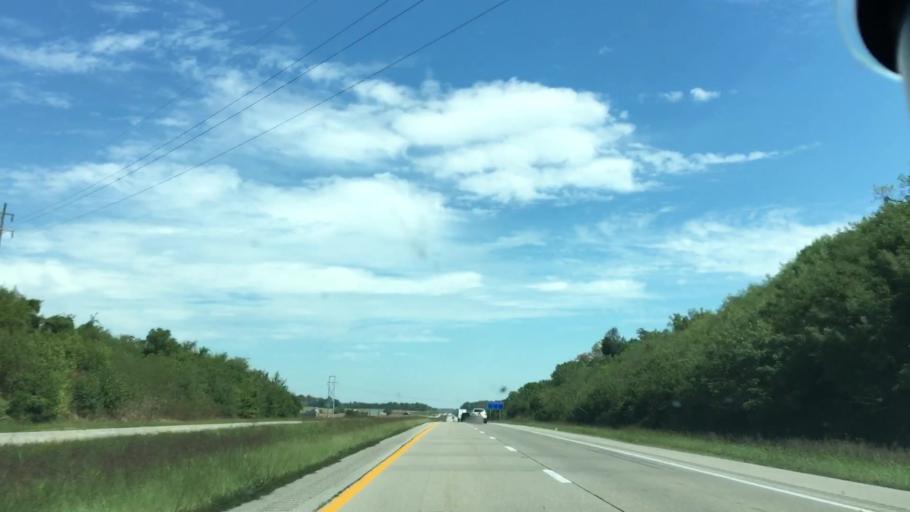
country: US
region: Kentucky
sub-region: Daviess County
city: Owensboro
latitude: 37.7526
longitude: -87.2779
